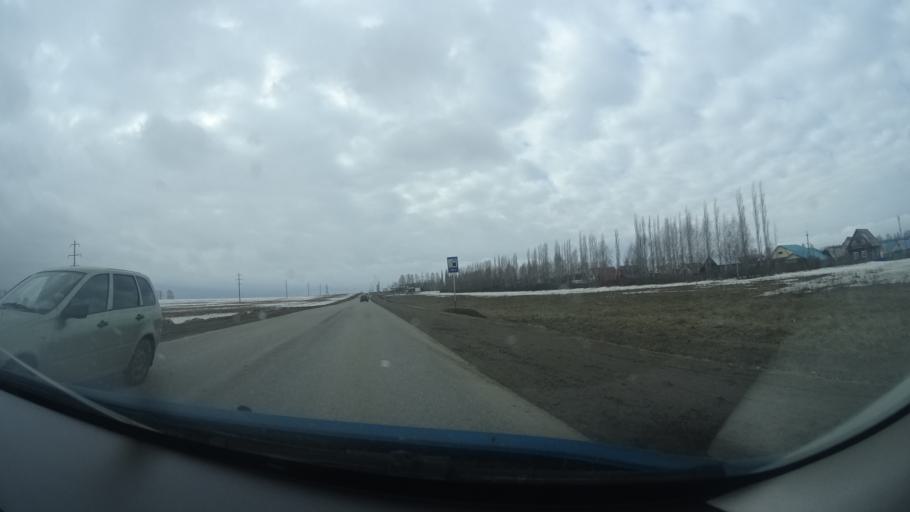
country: RU
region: Bashkortostan
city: Birsk
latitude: 55.4364
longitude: 55.5870
